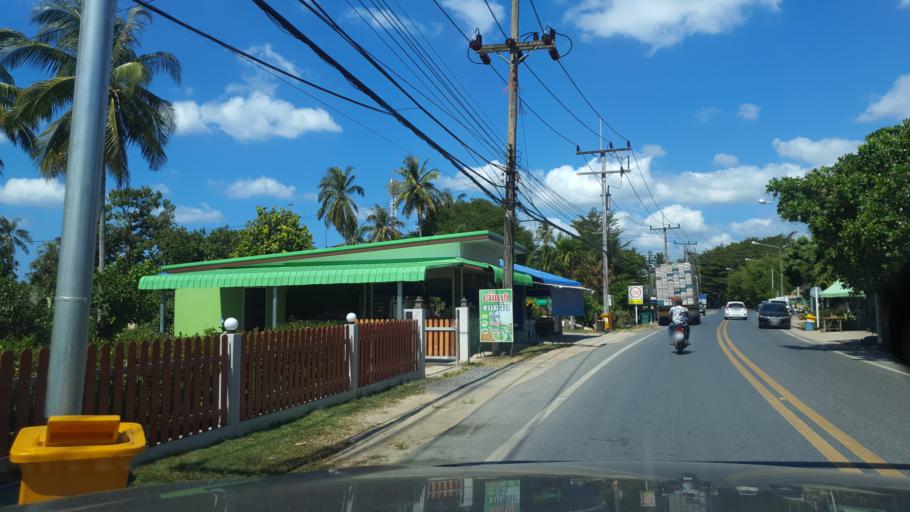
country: TH
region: Phuket
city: Thalang
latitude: 8.1283
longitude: 98.3080
